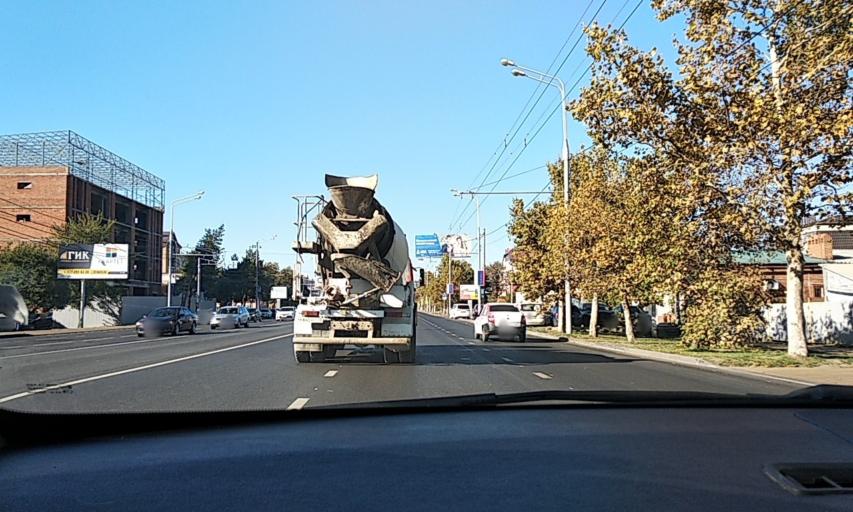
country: RU
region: Krasnodarskiy
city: Pashkovskiy
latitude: 45.0145
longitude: 39.0860
